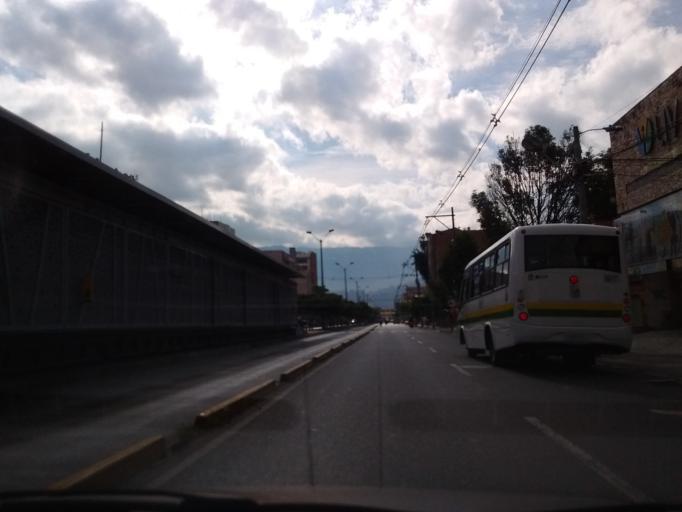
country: CO
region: Antioquia
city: Medellin
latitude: 6.2311
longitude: -75.6011
